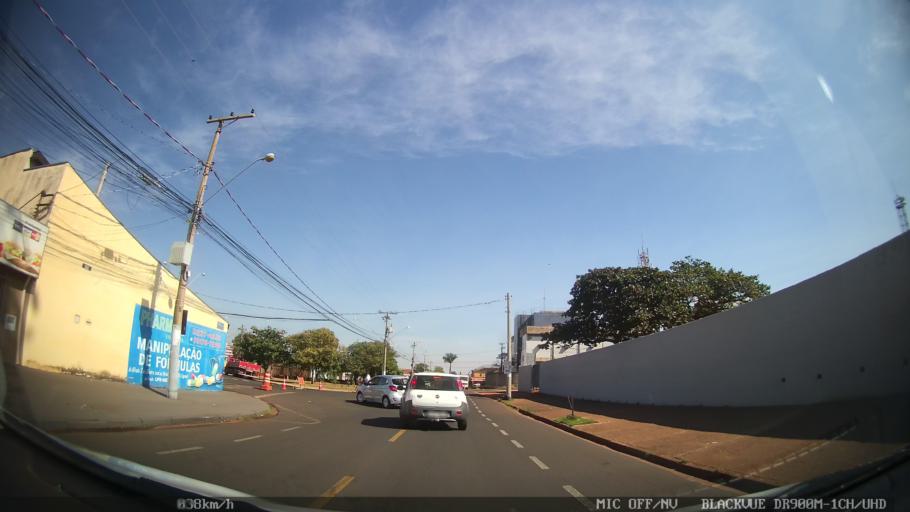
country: BR
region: Sao Paulo
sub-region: Sao Jose Do Rio Preto
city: Sao Jose do Rio Preto
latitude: -20.7863
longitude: -49.3988
